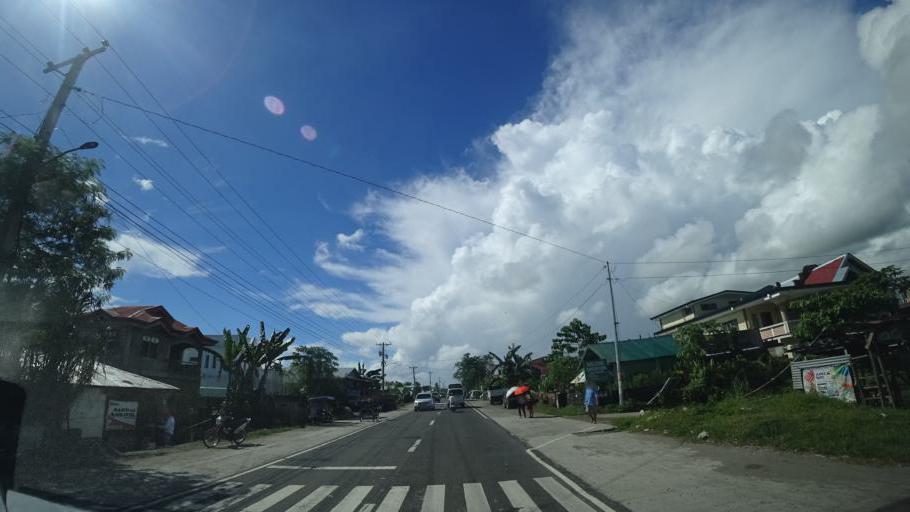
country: PH
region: Eastern Visayas
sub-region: Province of Leyte
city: Palo
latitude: 11.1484
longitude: 125.0010
